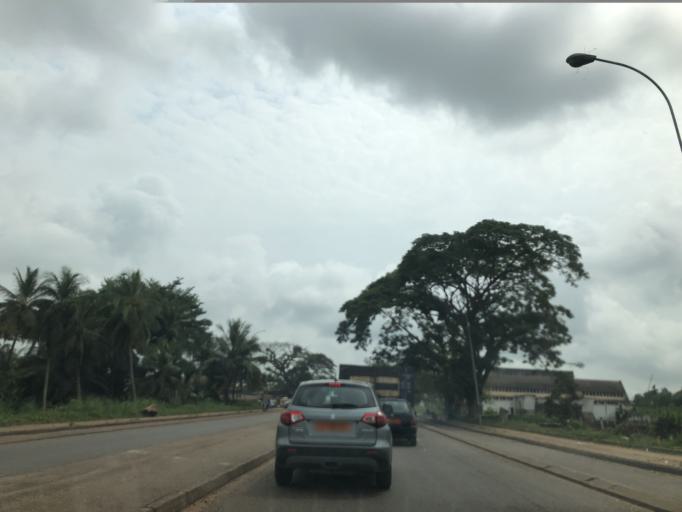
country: CM
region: Littoral
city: Edea
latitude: 3.7930
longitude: 10.1330
